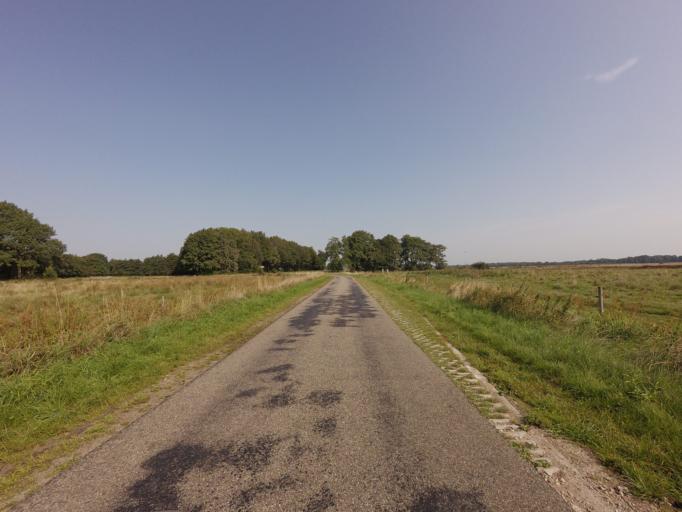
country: NL
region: Groningen
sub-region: Gemeente Groningen
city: Groningen
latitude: 53.1540
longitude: 6.5303
